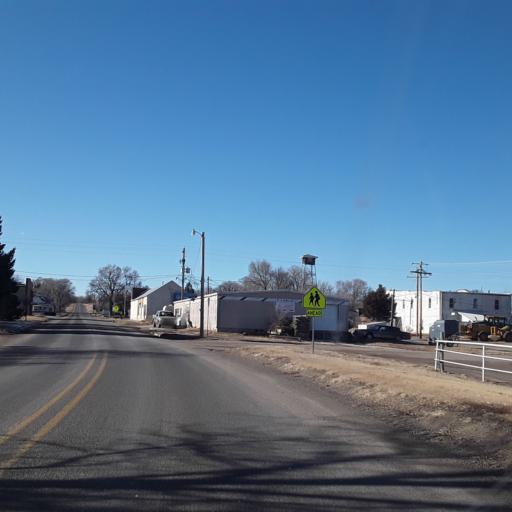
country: US
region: Nebraska
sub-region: Frontier County
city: Stockville
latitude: 40.6576
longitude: -100.6201
